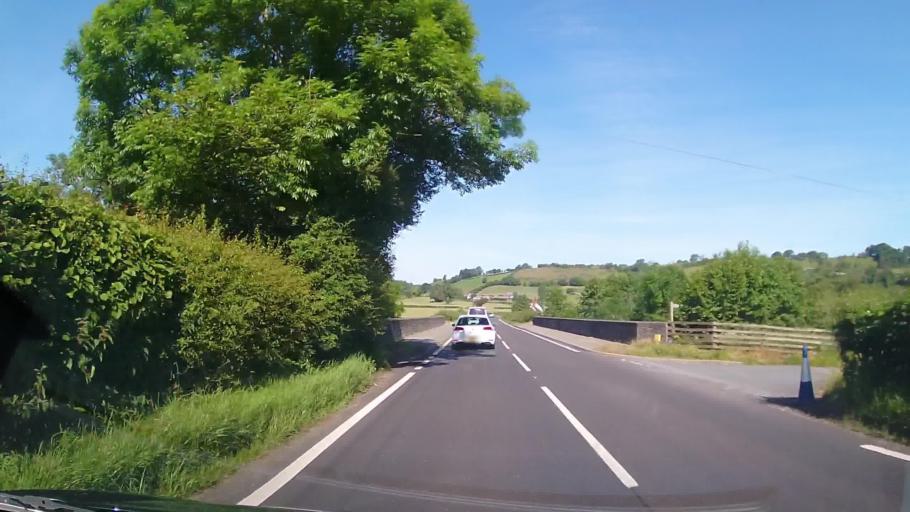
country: GB
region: Wales
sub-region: Sir Powys
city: Llanfyllin
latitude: 52.6620
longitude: -3.2777
